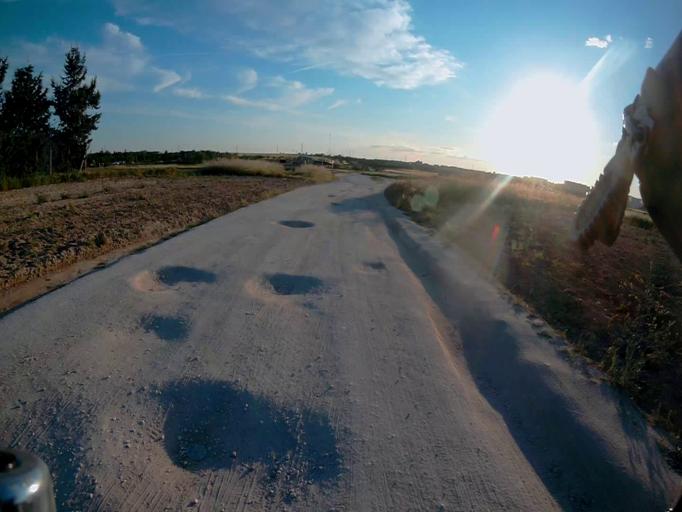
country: ES
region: Madrid
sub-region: Provincia de Madrid
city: Alcorcon
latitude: 40.3340
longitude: -3.7966
